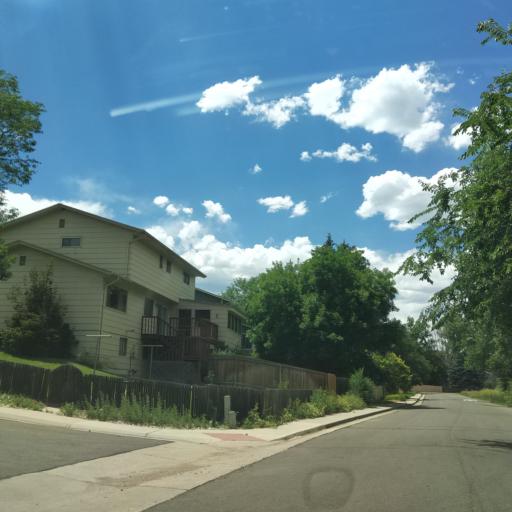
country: US
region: Colorado
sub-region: Jefferson County
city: Lakewood
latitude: 39.6882
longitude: -105.1016
